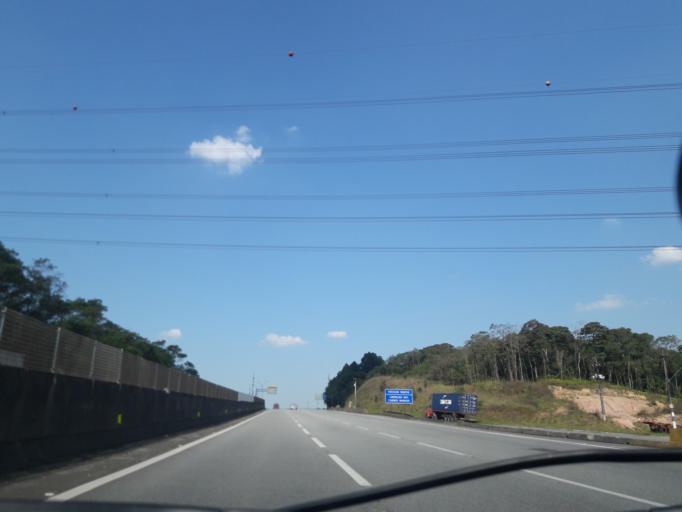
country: BR
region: Sao Paulo
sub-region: Sao Bernardo Do Campo
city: Sao Bernardo do Campo
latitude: -23.7863
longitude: -46.5229
